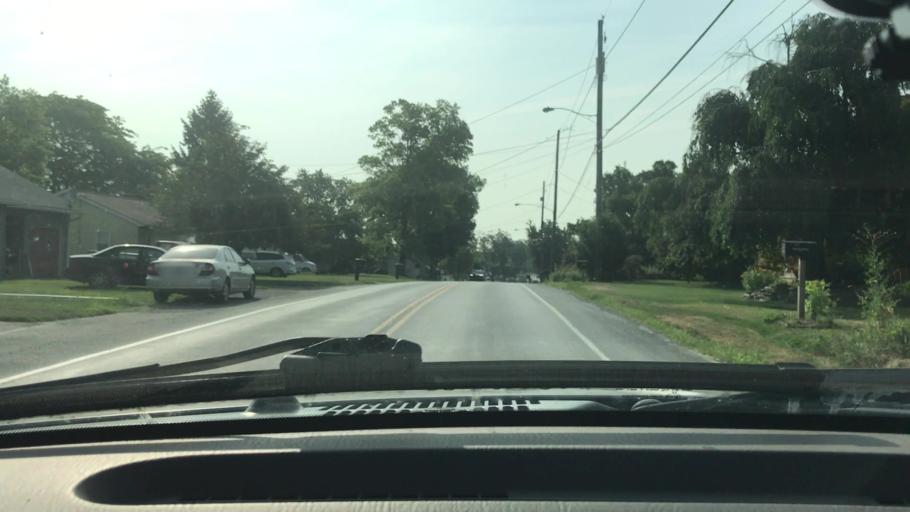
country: US
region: Pennsylvania
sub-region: Lancaster County
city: Rheems
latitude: 40.1302
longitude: -76.5690
